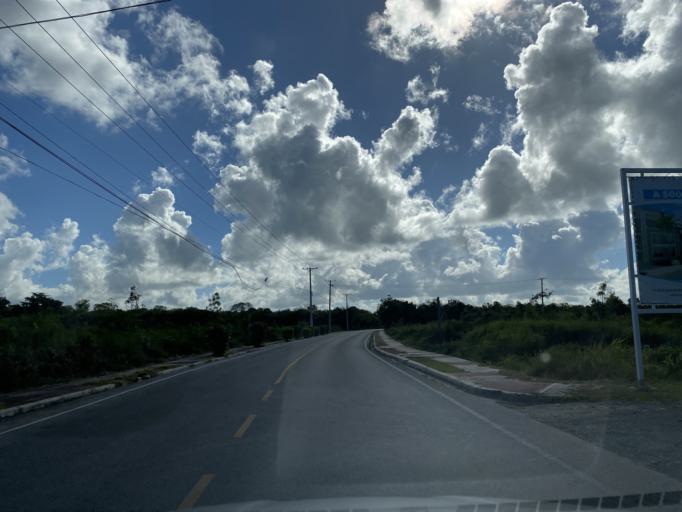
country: DO
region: La Altagracia
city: San Rafael del Yuma
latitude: 18.3428
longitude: -68.8146
